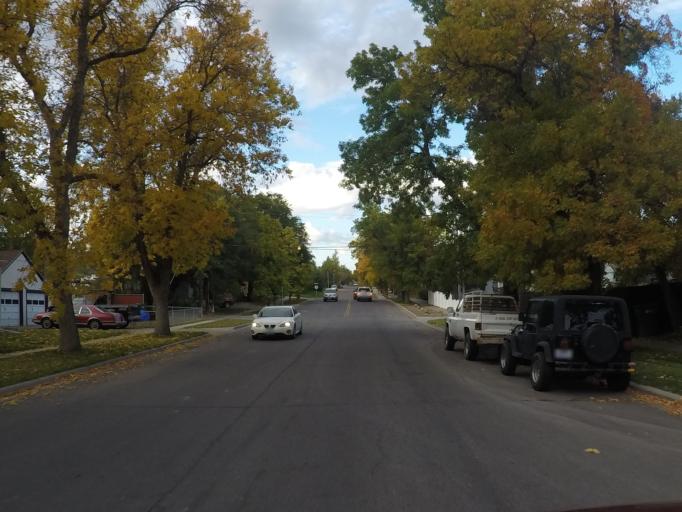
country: US
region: Montana
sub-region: Yellowstone County
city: Billings
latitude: 45.7831
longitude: -108.5306
